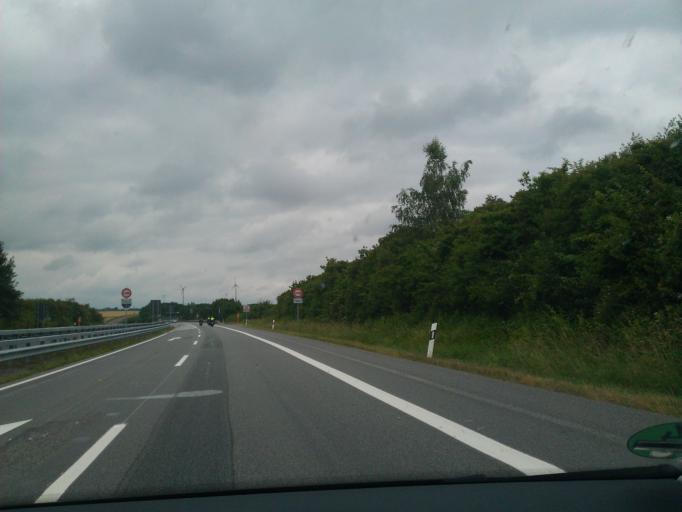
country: DE
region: Rheinland-Pfalz
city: Hermersberg
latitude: 49.3028
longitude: 7.6210
